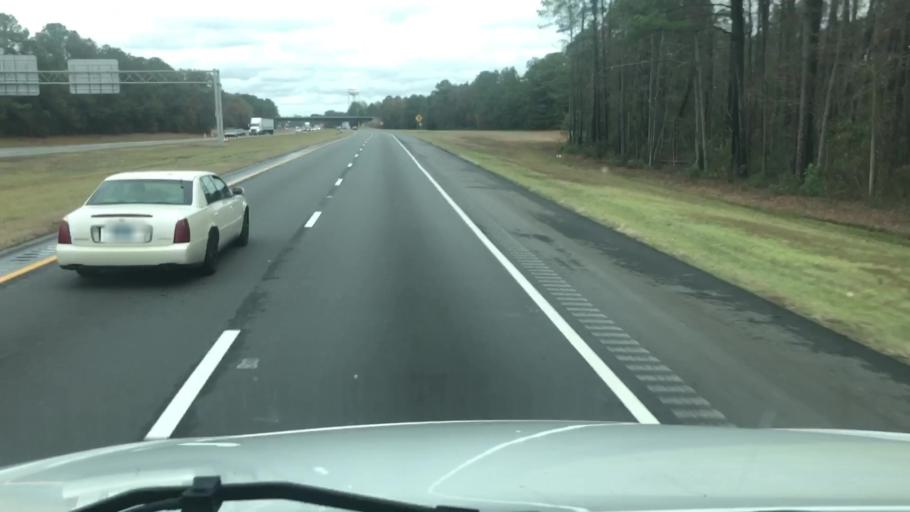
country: US
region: North Carolina
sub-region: Cumberland County
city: Eastover
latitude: 35.0911
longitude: -78.7809
